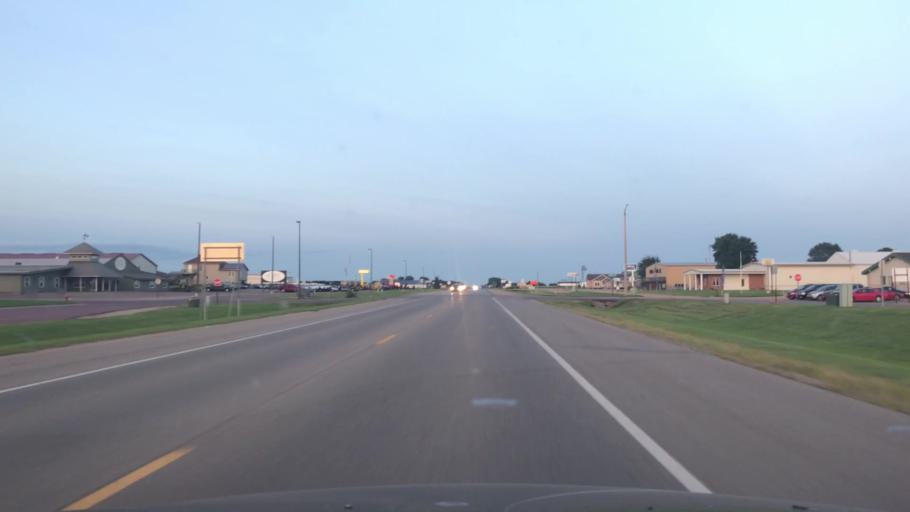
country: US
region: Minnesota
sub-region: Redwood County
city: Redwood Falls
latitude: 44.5414
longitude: -95.0875
